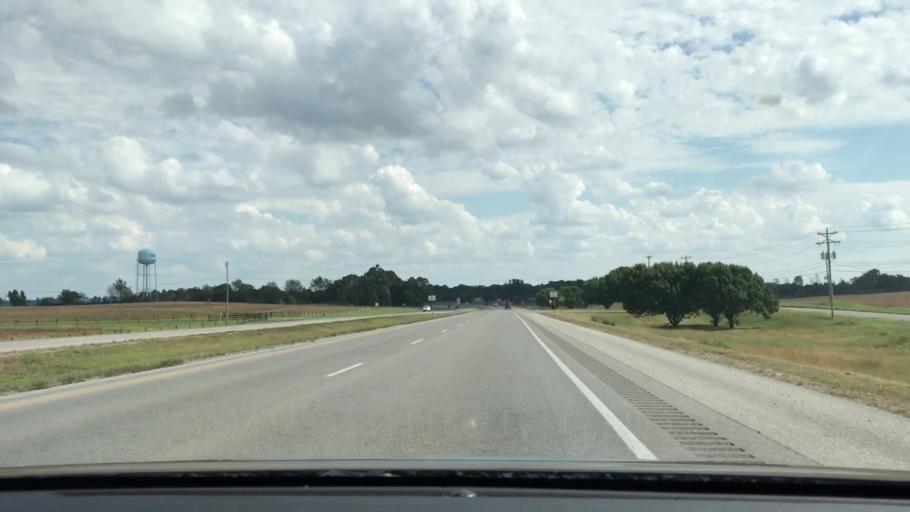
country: US
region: Kentucky
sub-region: Trigg County
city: Cadiz
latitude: 36.8676
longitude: -87.7855
